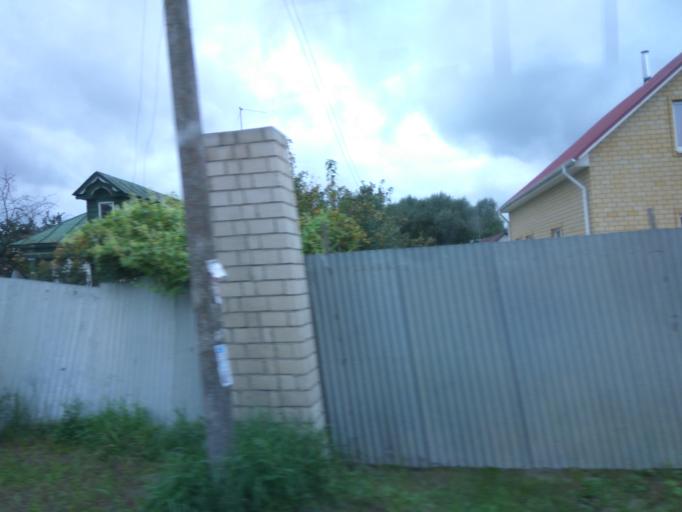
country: RU
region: Moskovskaya
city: Malyshevo
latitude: 55.5058
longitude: 38.3438
